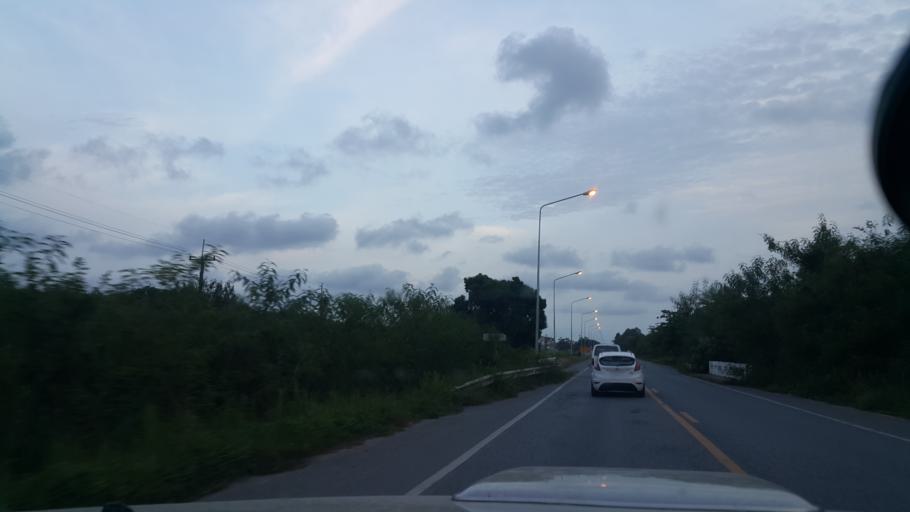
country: TH
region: Rayong
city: Ban Chang
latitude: 12.7160
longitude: 100.9976
